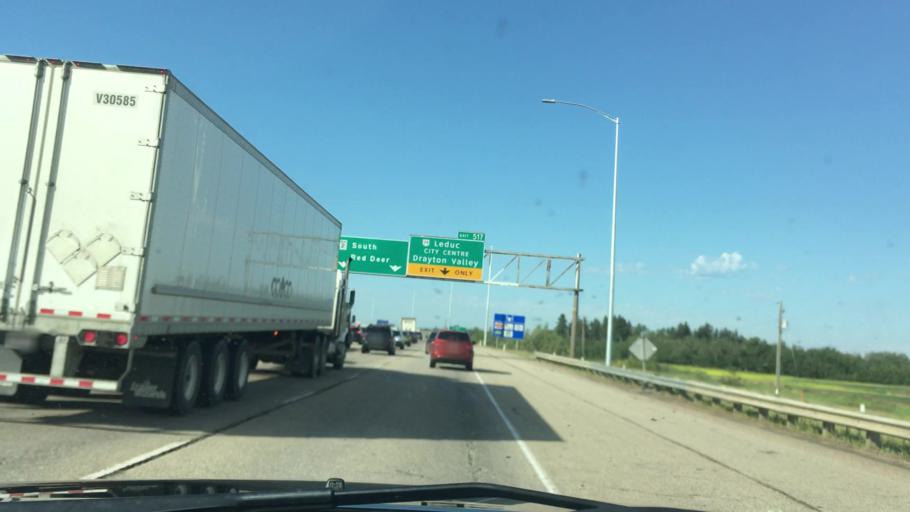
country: CA
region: Alberta
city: Leduc
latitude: 53.2748
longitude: -113.5571
